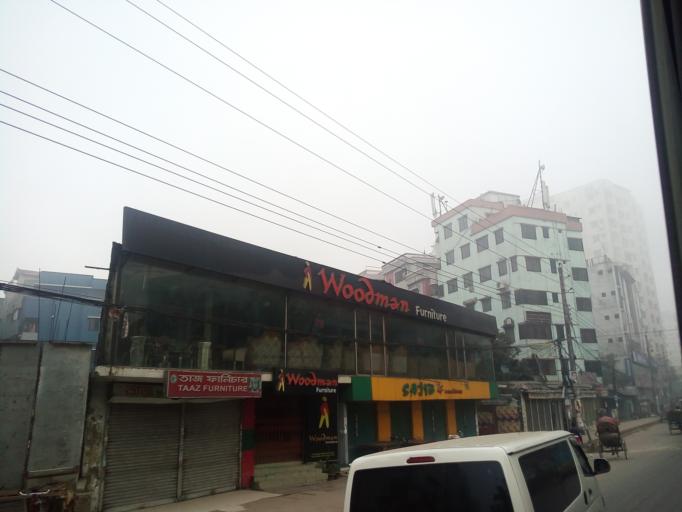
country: BD
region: Dhaka
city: Azimpur
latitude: 23.7872
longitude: 90.3770
